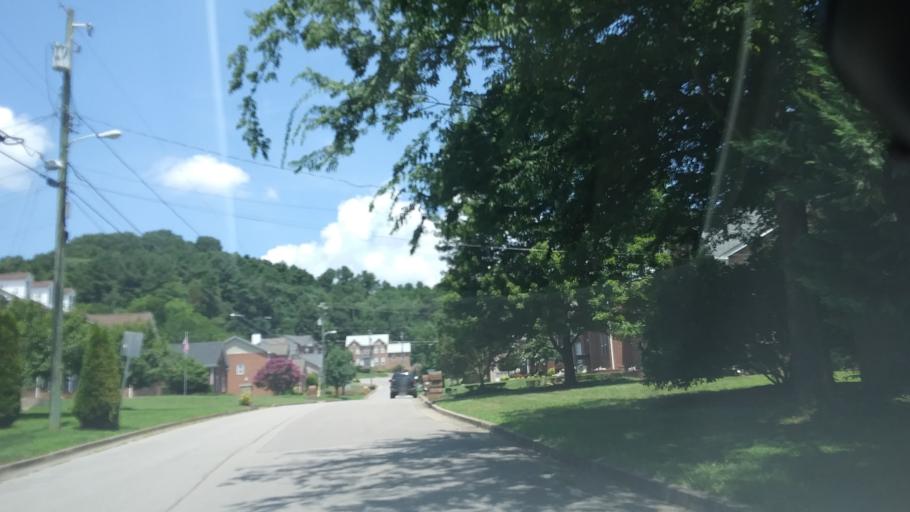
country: US
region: Tennessee
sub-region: Davidson County
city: Belle Meade
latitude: 36.0894
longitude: -86.9439
